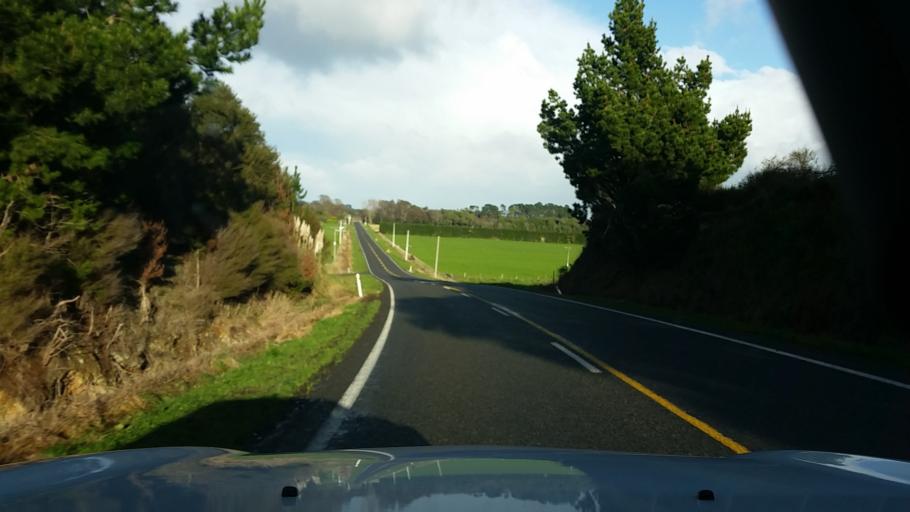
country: NZ
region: Wellington
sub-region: South Wairarapa District
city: Waipawa
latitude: -41.3127
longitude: 175.2641
